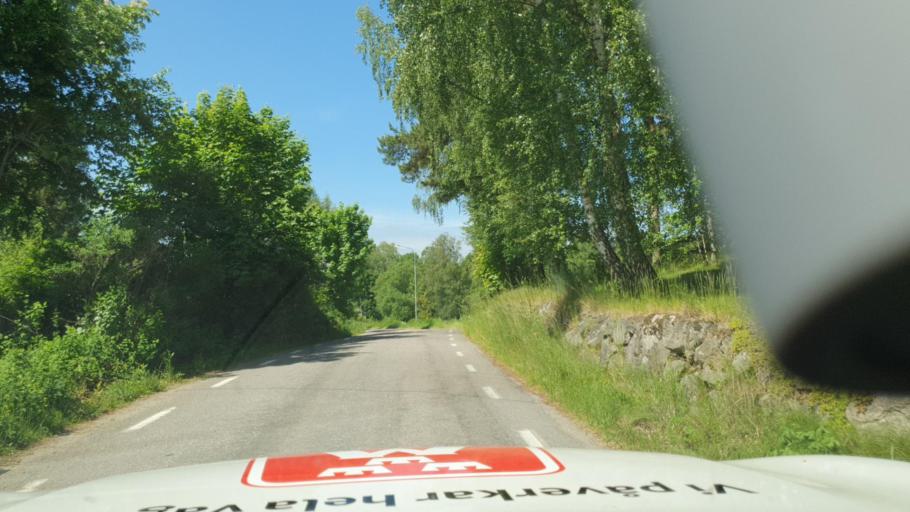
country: SE
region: Vaestra Goetaland
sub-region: Herrljunga Kommun
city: Herrljunga
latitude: 58.1419
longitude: 13.0287
